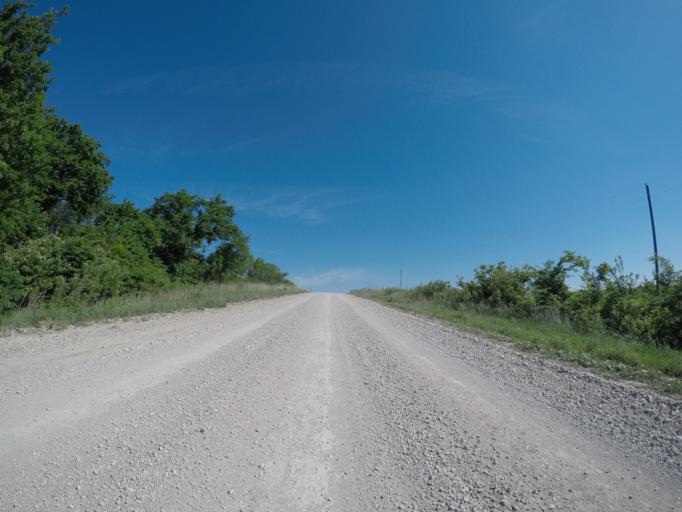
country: US
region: Kansas
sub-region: Wabaunsee County
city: Alma
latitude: 38.9737
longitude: -96.1139
